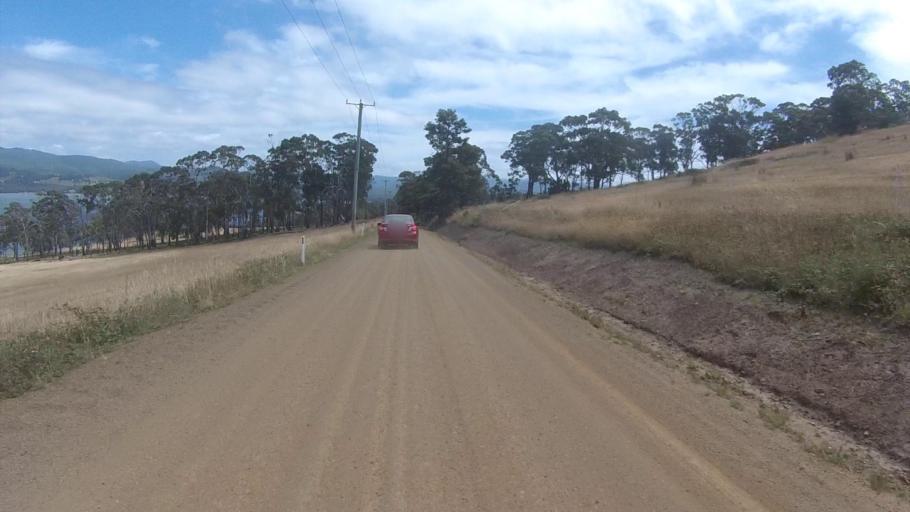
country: AU
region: Tasmania
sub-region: Kingborough
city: Blackmans Bay
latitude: -43.0543
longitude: 147.3146
